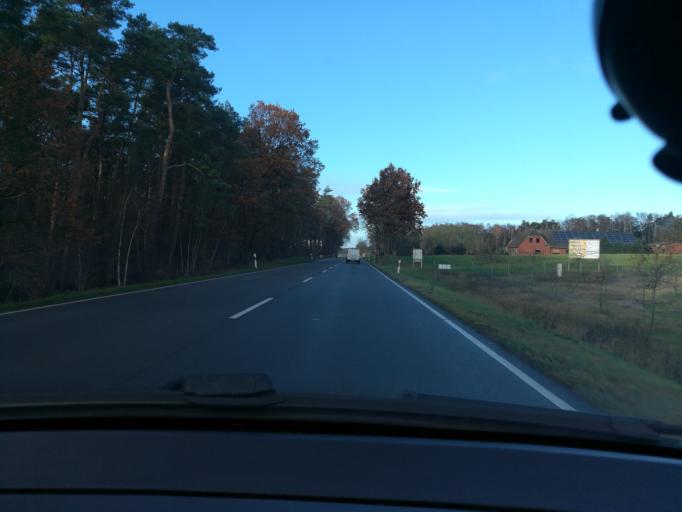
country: DE
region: Lower Saxony
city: Kirchdorf
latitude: 52.5474
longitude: 8.8632
